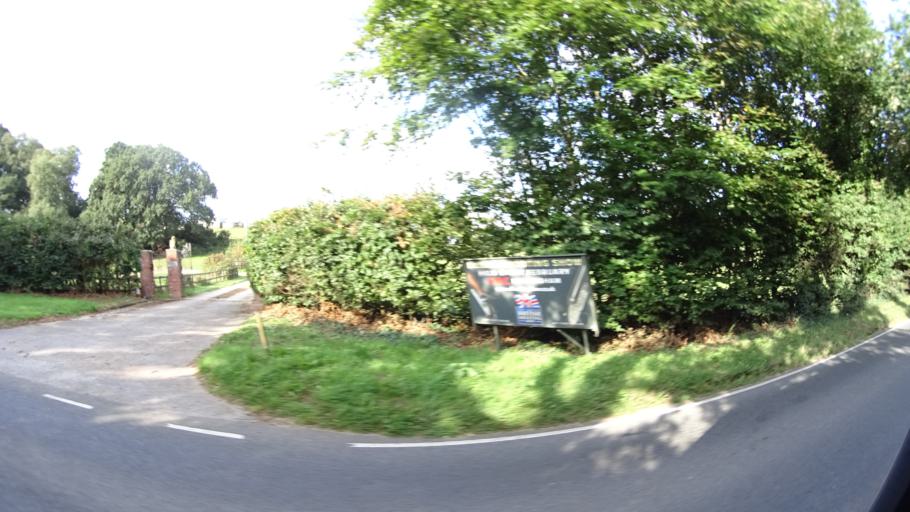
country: GB
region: England
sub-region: Dorset
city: Lytchett Matravers
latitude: 50.7734
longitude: -2.0681
